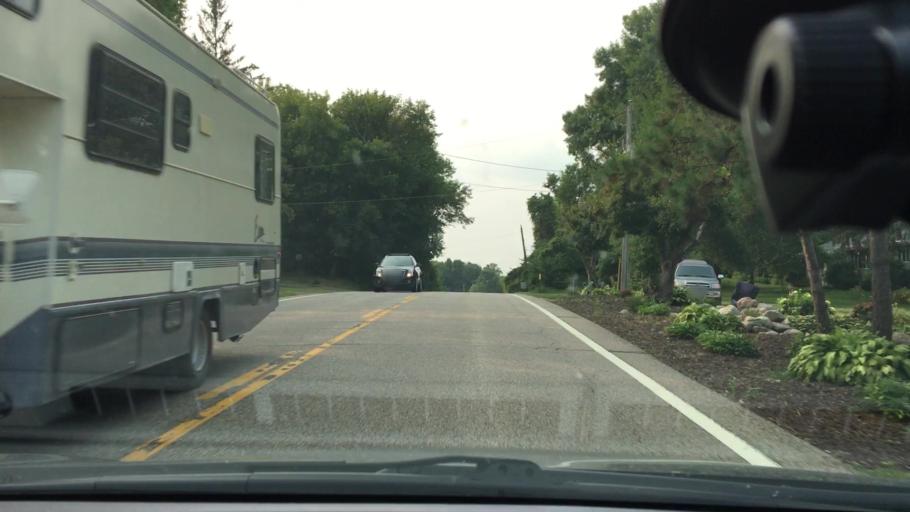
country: US
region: Minnesota
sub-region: Hennepin County
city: Dayton
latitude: 45.2264
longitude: -93.4905
